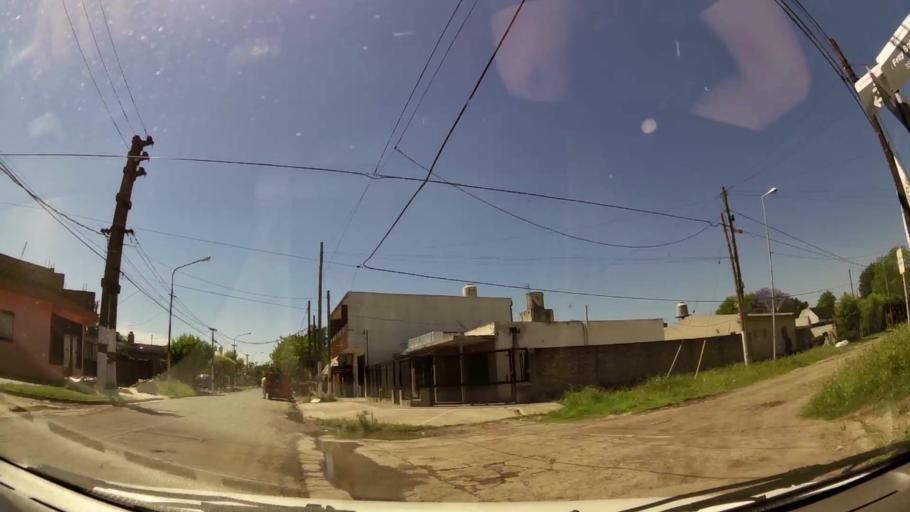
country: AR
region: Buenos Aires
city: Ituzaingo
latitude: -34.6764
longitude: -58.6587
